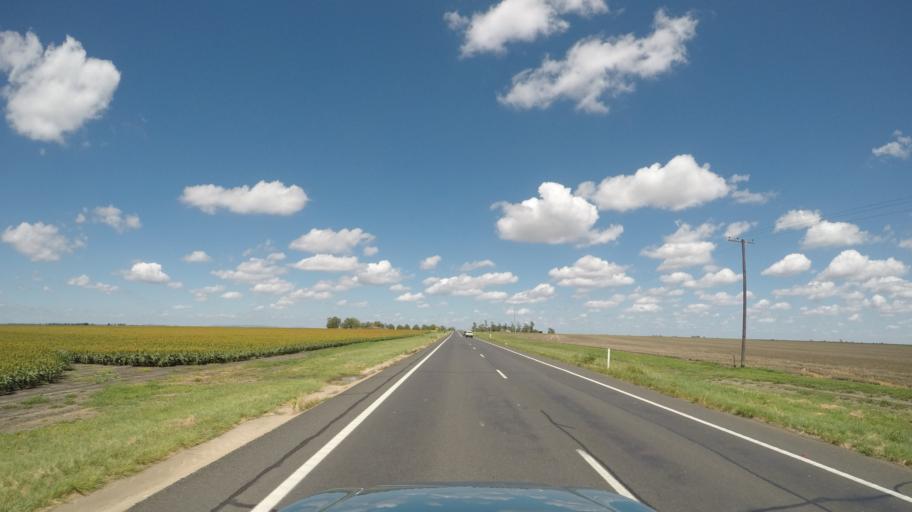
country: AU
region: Queensland
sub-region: Toowoomba
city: Oakey
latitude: -27.7568
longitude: 151.5005
